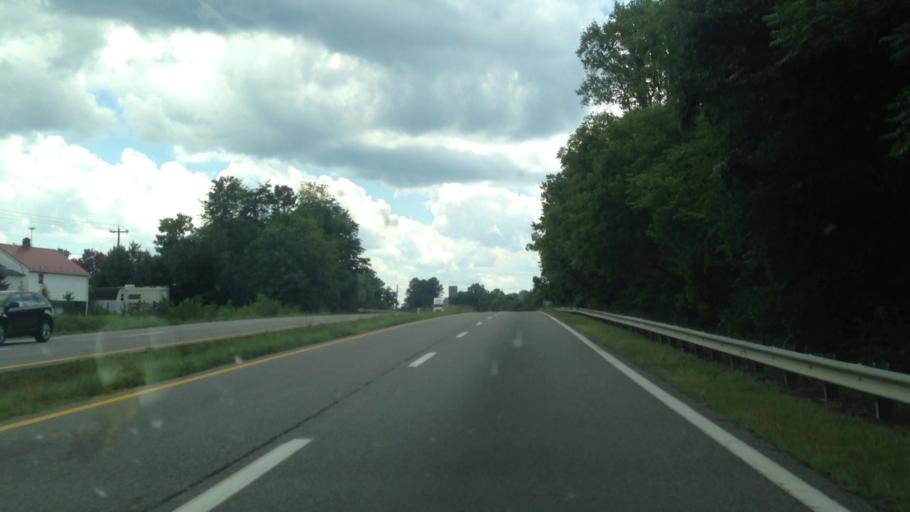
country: US
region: Virginia
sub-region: Henry County
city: Horse Pasture
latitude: 36.5732
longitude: -79.8702
